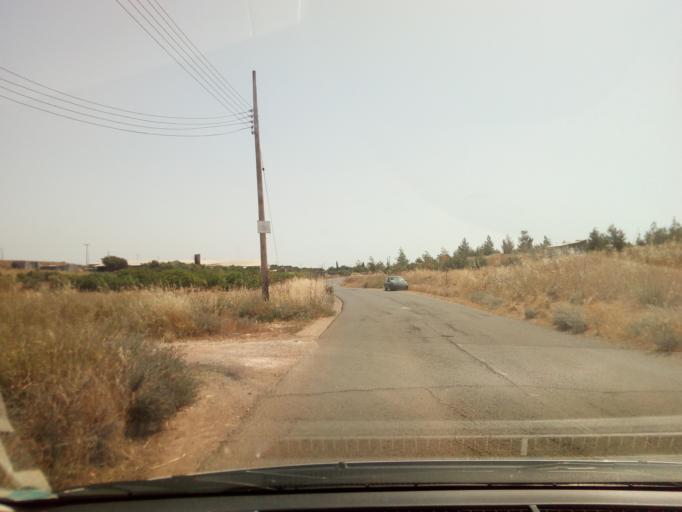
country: CY
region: Larnaka
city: Xylotymbou
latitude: 34.9862
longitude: 33.7974
